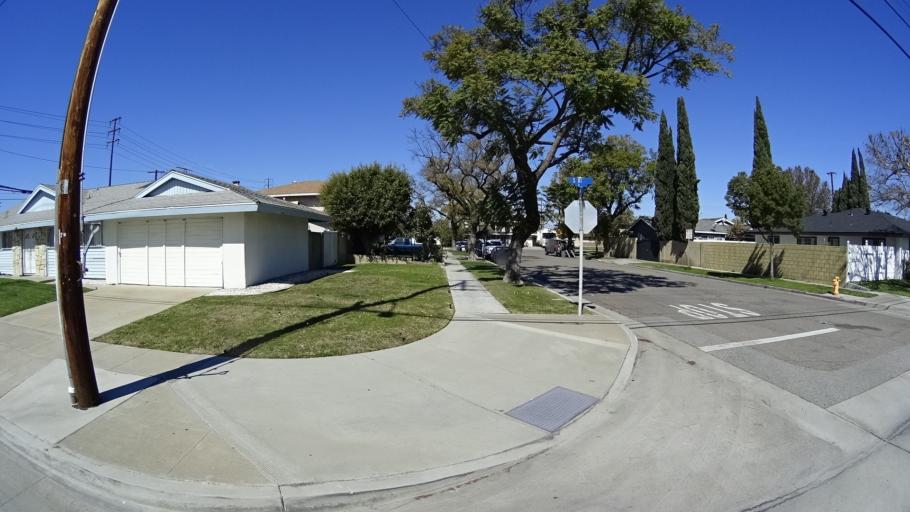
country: US
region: California
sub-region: Orange County
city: Anaheim
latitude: 33.8295
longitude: -117.8989
